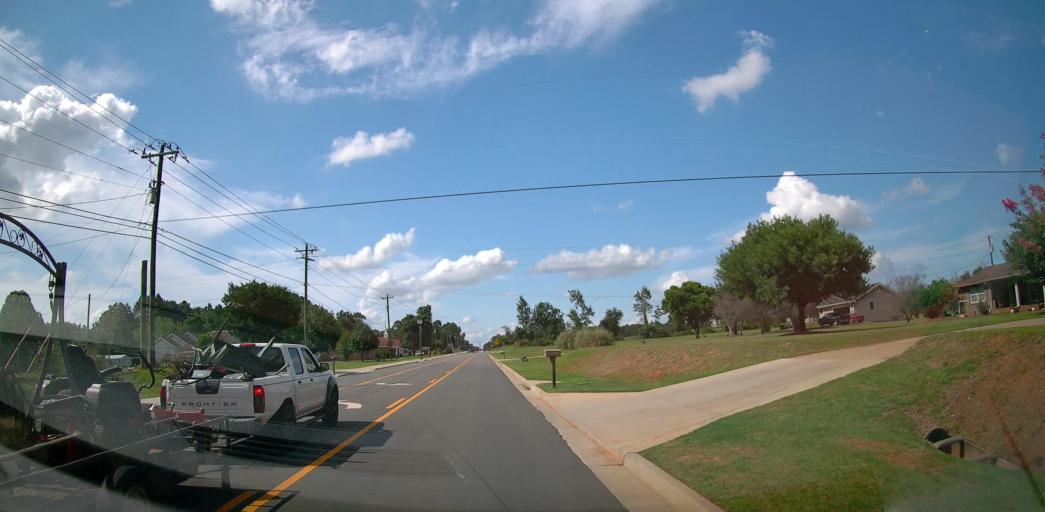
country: US
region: Georgia
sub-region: Houston County
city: Perry
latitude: 32.5200
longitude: -83.6910
